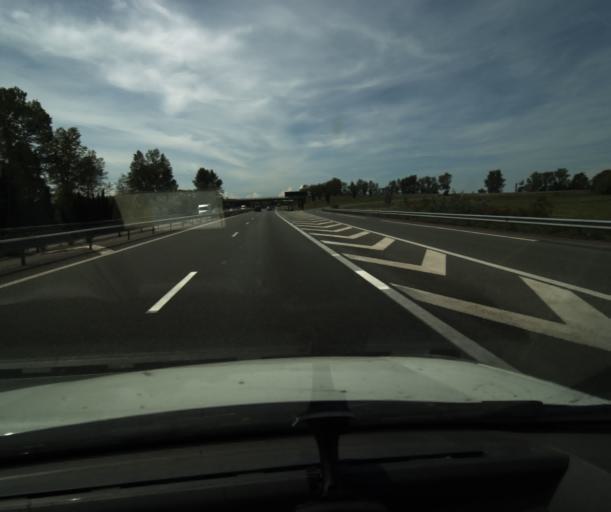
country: FR
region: Languedoc-Roussillon
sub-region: Departement de l'Aude
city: Villeneuve-la-Comptal
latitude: 43.2878
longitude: 1.9477
